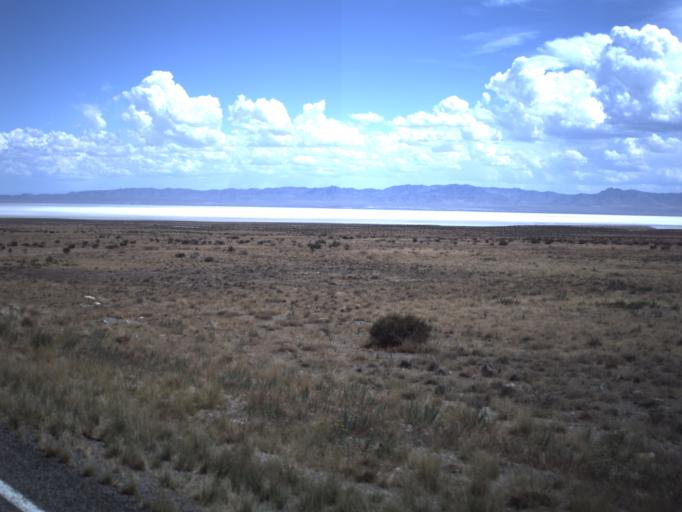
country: US
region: Utah
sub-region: Beaver County
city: Milford
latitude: 39.0538
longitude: -113.2633
